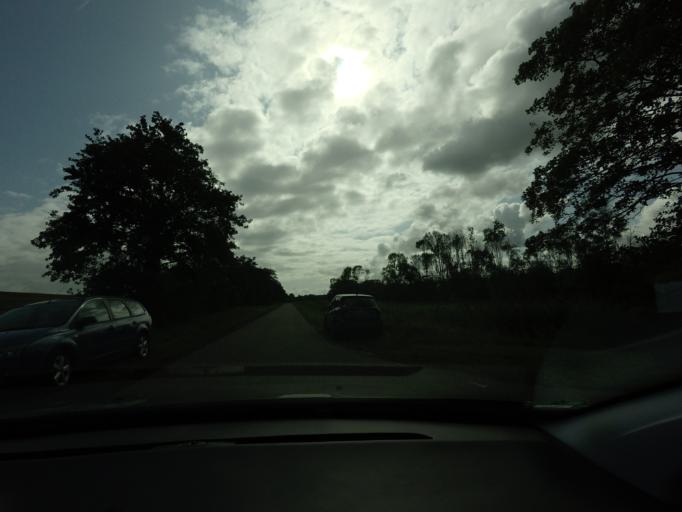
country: NL
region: North Holland
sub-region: Gemeente Hollands Kroon
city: Den Oever
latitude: 52.8954
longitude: 5.0710
